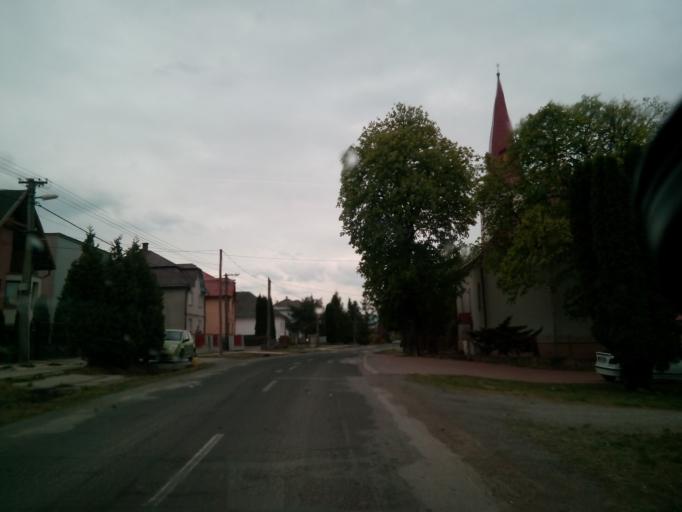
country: SK
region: Kosicky
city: Kosice
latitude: 48.7425
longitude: 21.4393
